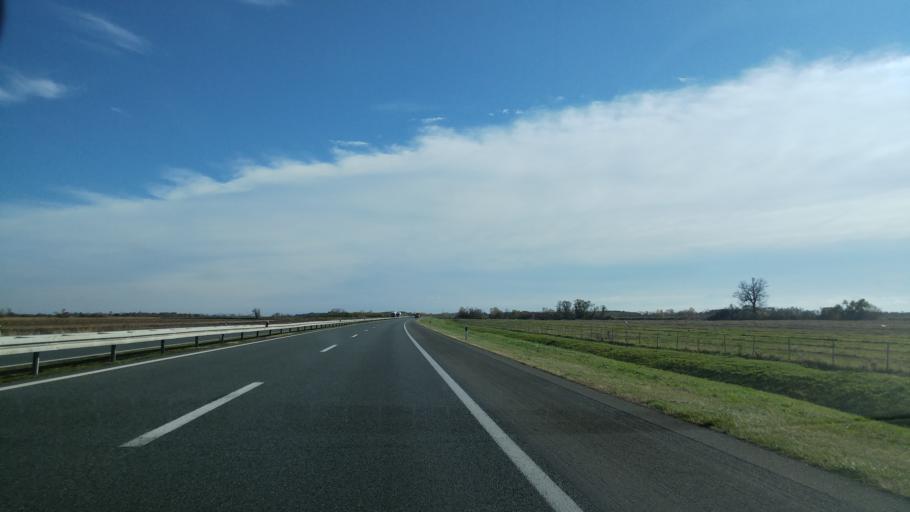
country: HR
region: Brodsko-Posavska
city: Okucani
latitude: 45.2591
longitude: 17.1666
